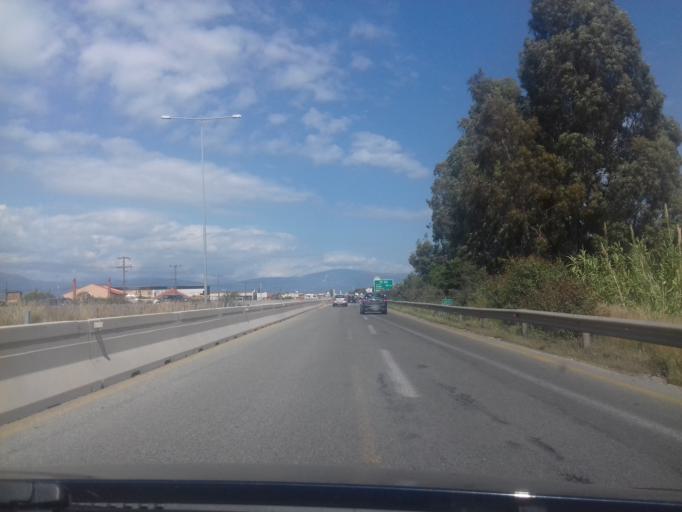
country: GR
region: West Greece
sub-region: Nomos Achaias
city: Rio
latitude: 38.2914
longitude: 21.7809
